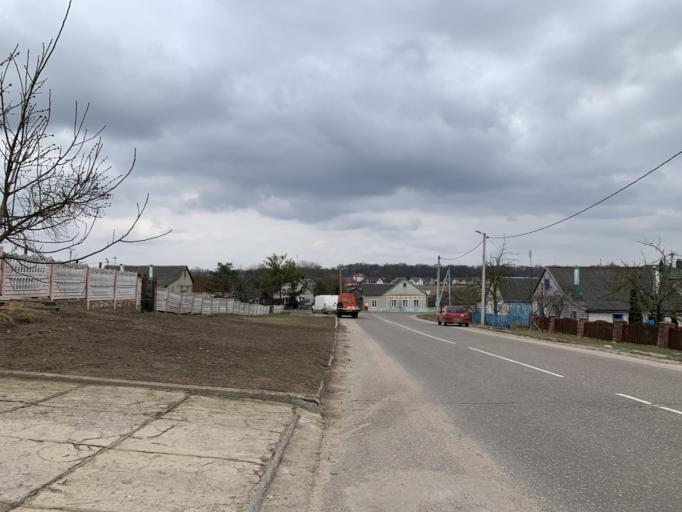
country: BY
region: Minsk
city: Nyasvizh
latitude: 53.2318
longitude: 26.6819
